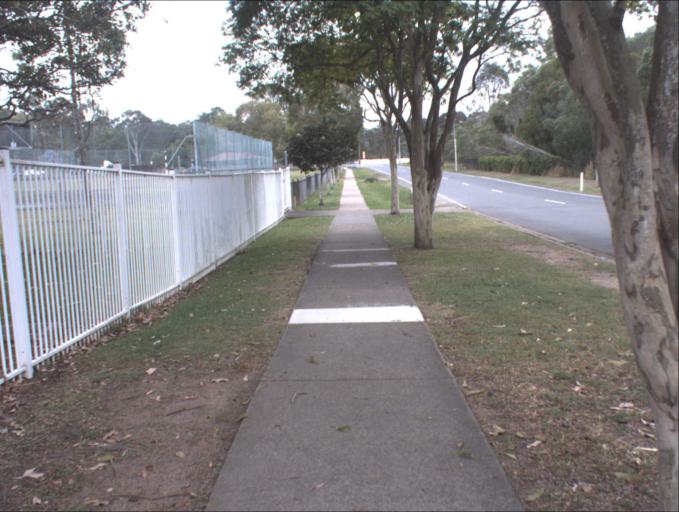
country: AU
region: Queensland
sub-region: Gold Coast
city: Yatala
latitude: -27.6797
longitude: 153.2360
